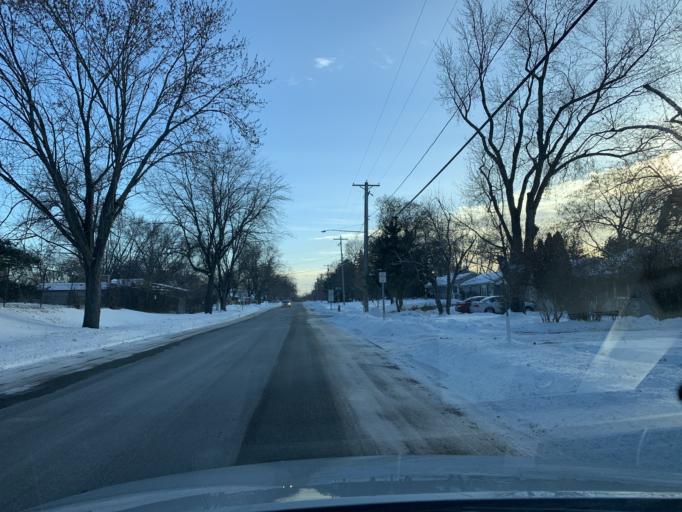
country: US
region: Minnesota
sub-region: Hennepin County
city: Minnetonka Mills
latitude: 44.9616
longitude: -93.3963
